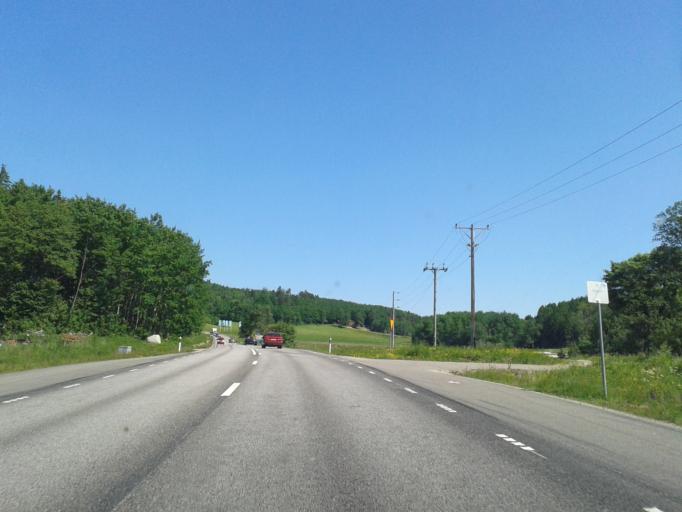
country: SE
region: Vaestra Goetaland
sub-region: Orust
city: Henan
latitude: 58.3242
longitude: 11.6841
